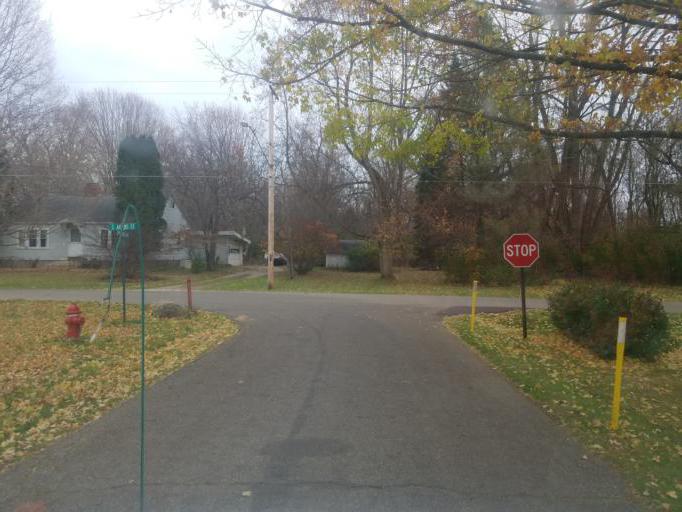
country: US
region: Ohio
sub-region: Knox County
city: Mount Vernon
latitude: 40.3905
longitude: -82.4948
